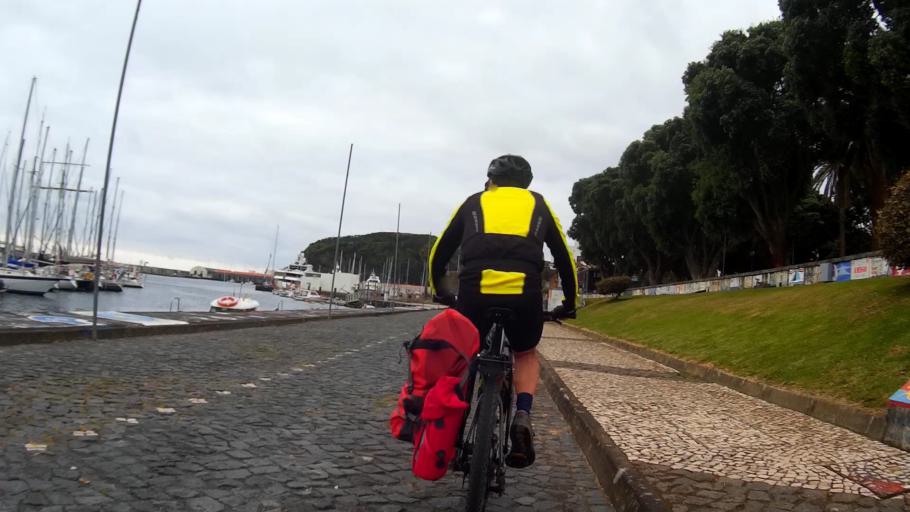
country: PT
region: Azores
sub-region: Horta
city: Horta
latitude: 38.5330
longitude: -28.6261
